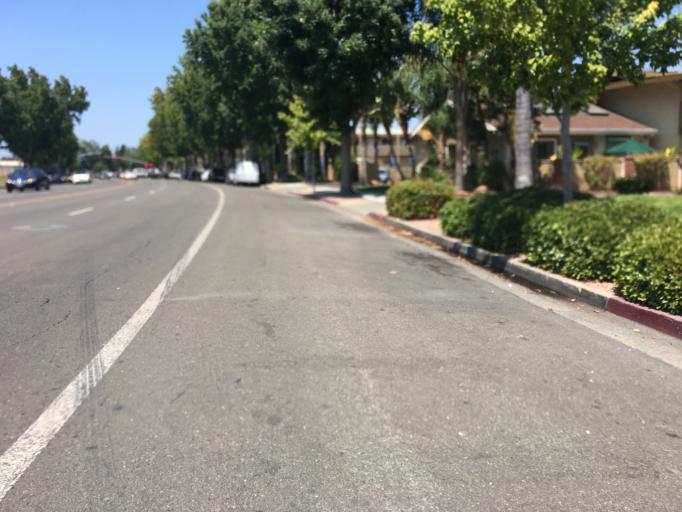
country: US
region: California
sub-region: Santa Clara County
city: Los Altos
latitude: 37.4004
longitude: -122.1020
